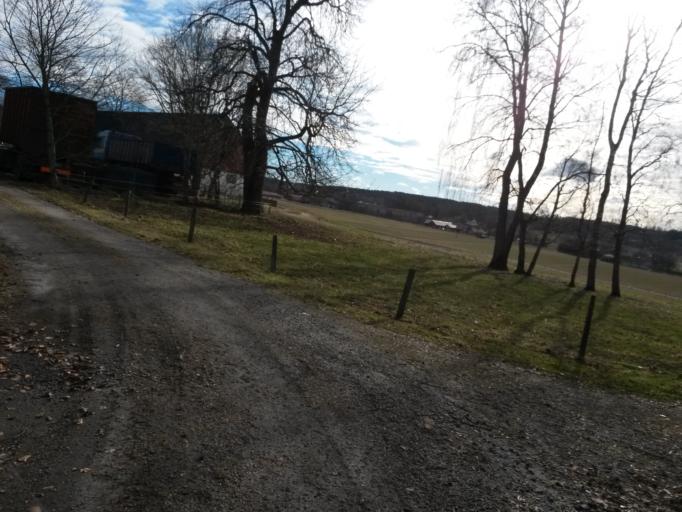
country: SE
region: Vaestra Goetaland
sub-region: Vargarda Kommun
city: Jonstorp
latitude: 57.9792
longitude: 12.6519
